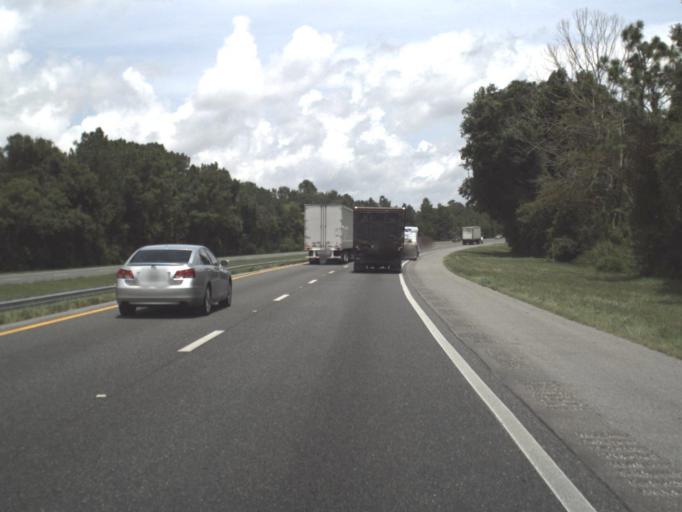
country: US
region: Florida
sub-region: Hernando County
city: Hill 'n Dale
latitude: 28.5591
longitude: -82.2368
